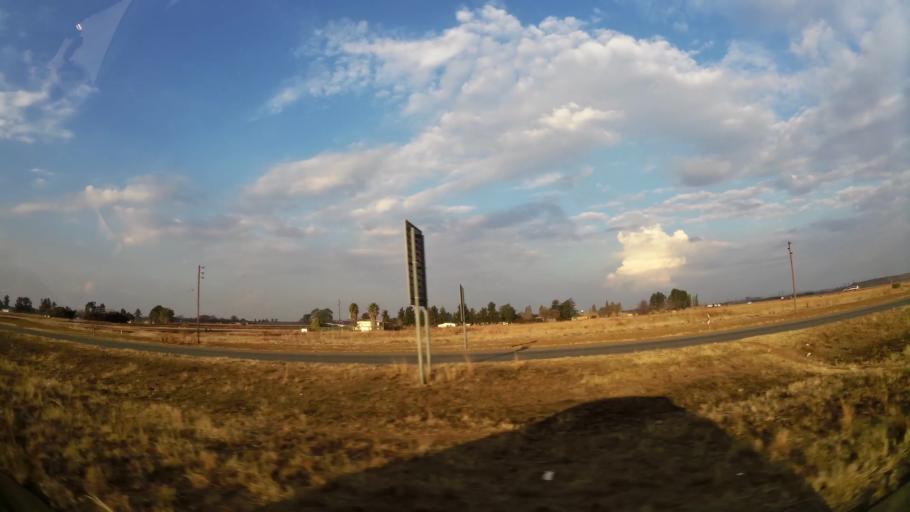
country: ZA
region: Gauteng
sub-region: Sedibeng District Municipality
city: Vanderbijlpark
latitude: -26.6159
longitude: 27.8136
